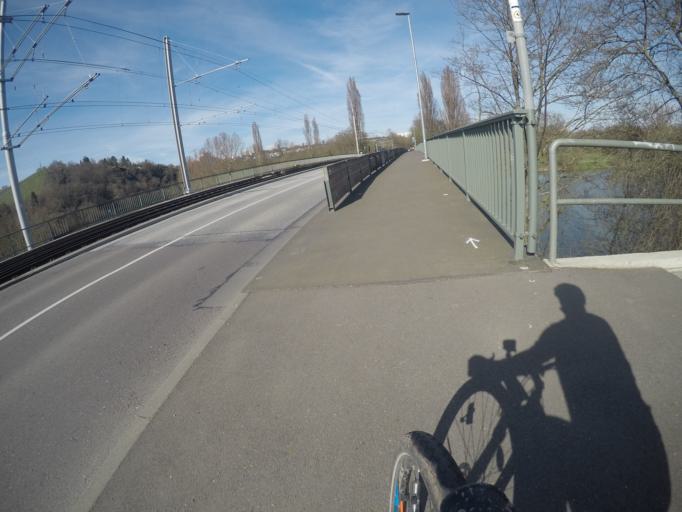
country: DE
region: Baden-Wuerttemberg
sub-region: Regierungsbezirk Stuttgart
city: Stuttgart Muehlhausen
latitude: 48.8259
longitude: 9.2109
